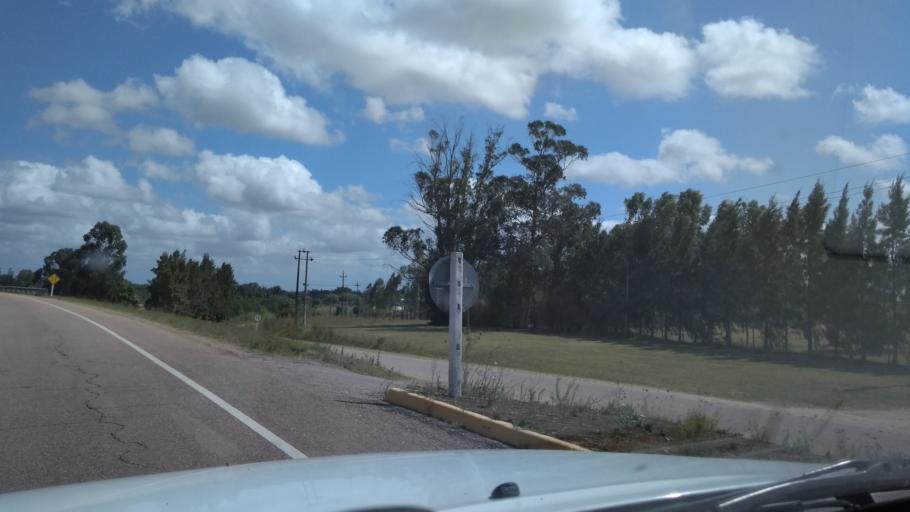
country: UY
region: Canelones
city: Sauce
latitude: -34.6380
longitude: -56.0527
